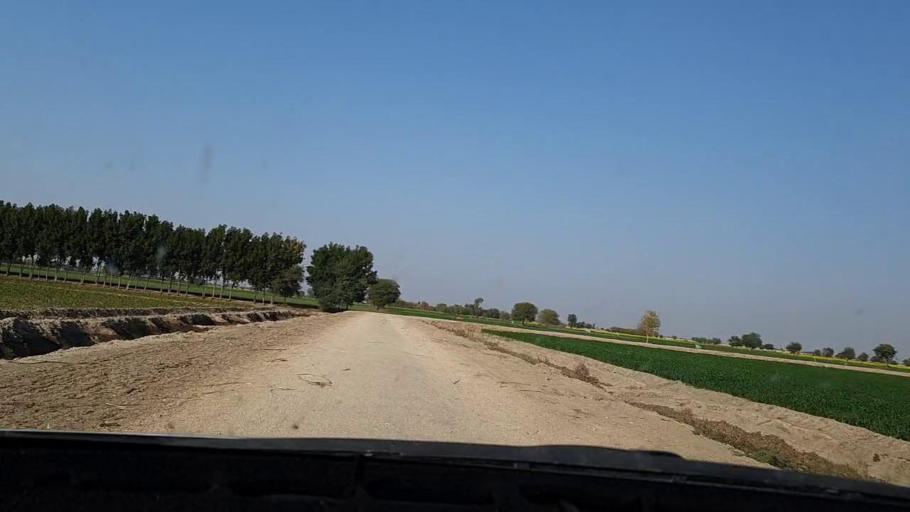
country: PK
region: Sindh
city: Tando Mittha Khan
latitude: 25.8273
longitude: 69.3064
